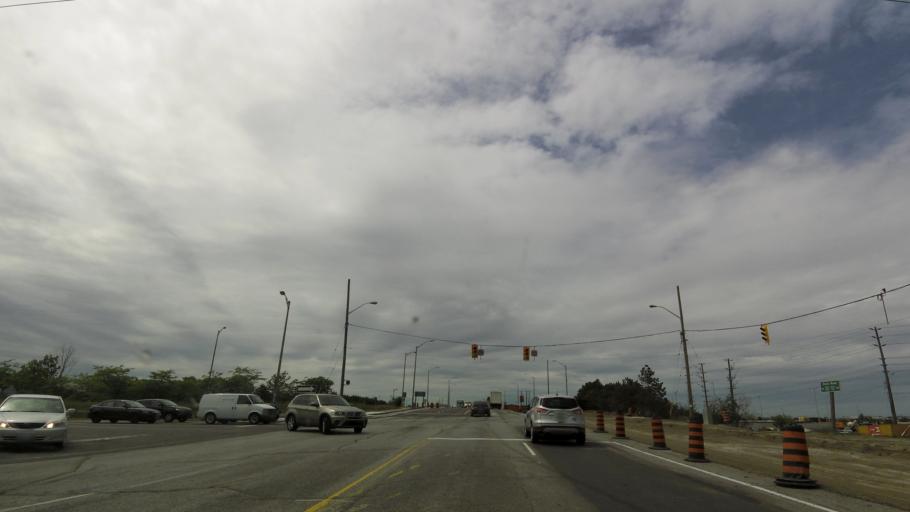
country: CA
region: Ontario
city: Etobicoke
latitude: 43.6467
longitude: -79.6357
